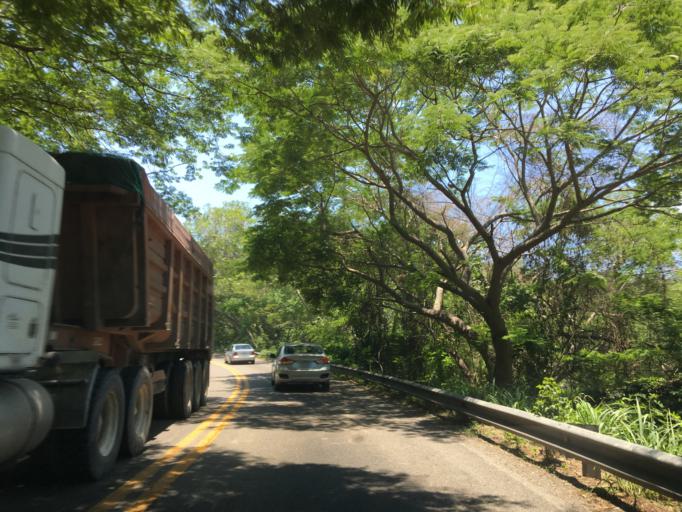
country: MX
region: Nayarit
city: Bucerias
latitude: 20.8246
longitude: -105.4048
